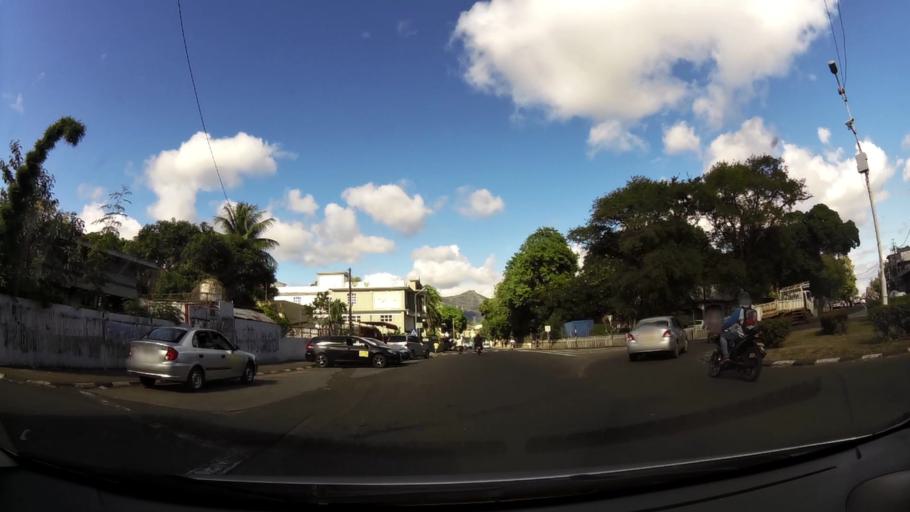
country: MU
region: Pamplemousses
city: Le Hochet
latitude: -20.1466
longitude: 57.5235
